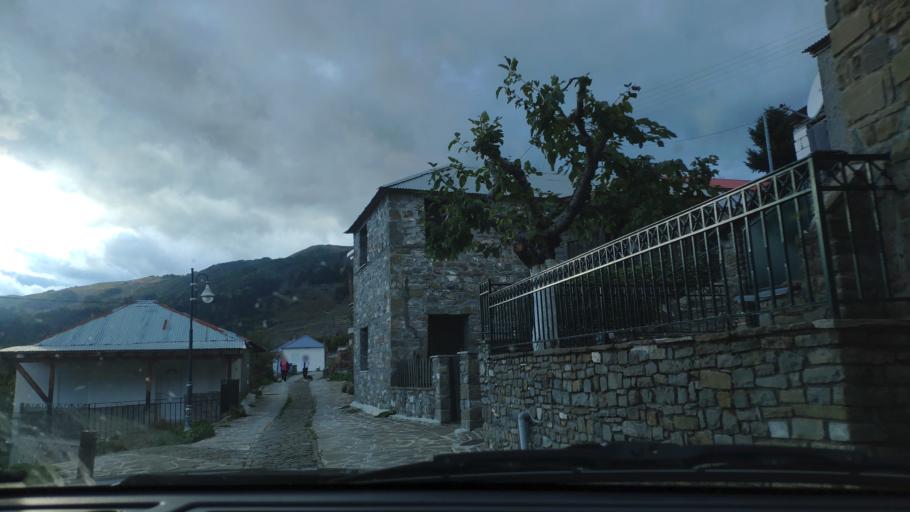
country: AL
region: Korce
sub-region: Rrethi i Kolonjes
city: Erseke
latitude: 40.3107
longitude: 20.8552
